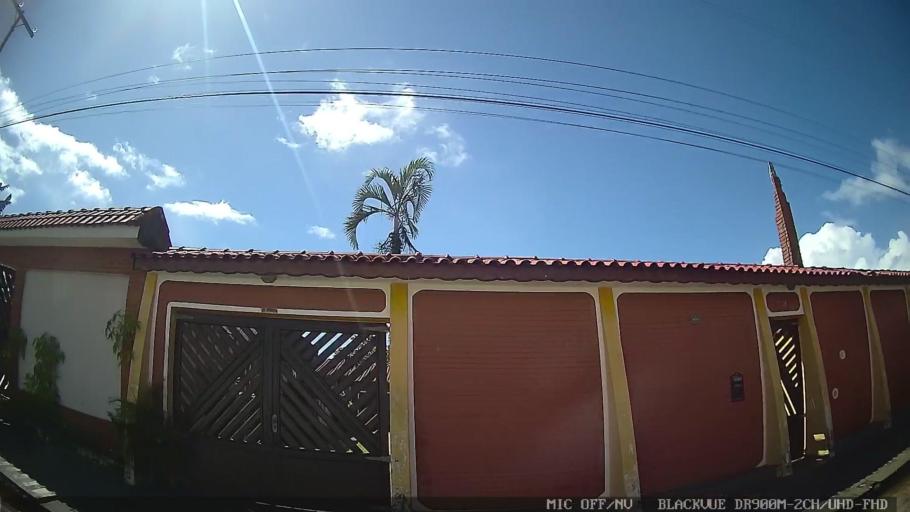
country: BR
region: Sao Paulo
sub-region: Itanhaem
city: Itanhaem
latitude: -24.2329
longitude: -46.8746
